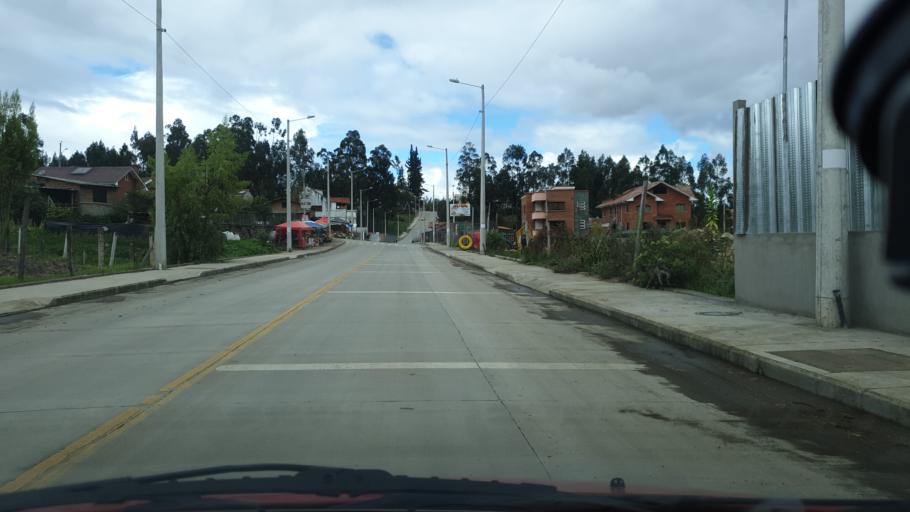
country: EC
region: Azuay
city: Cuenca
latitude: -2.8816
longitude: -79.0565
